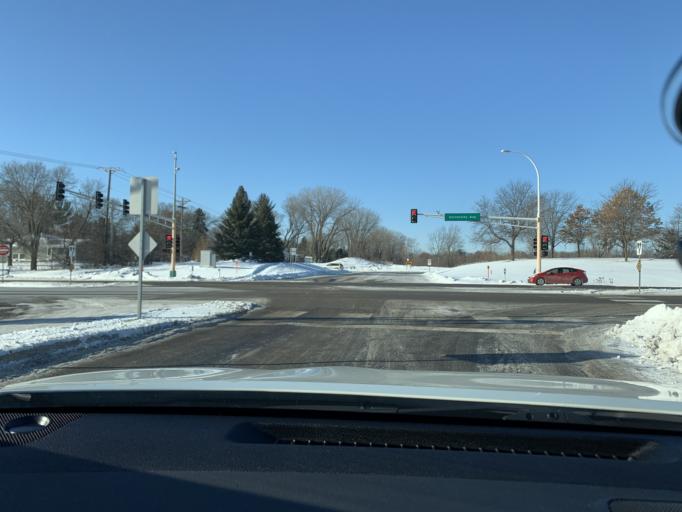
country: US
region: Minnesota
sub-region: Anoka County
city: Fridley
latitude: 45.0937
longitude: -93.2632
